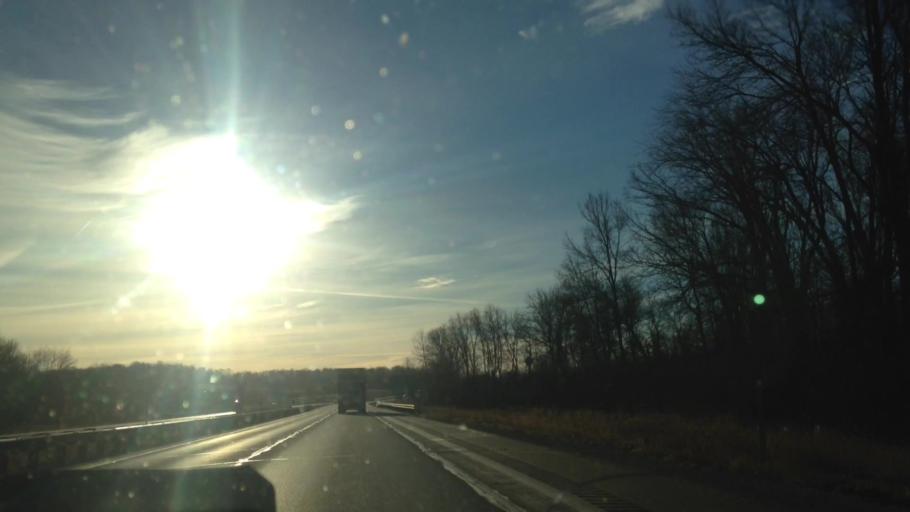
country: US
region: Wisconsin
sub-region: Washington County
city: Slinger
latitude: 43.4385
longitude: -88.3462
